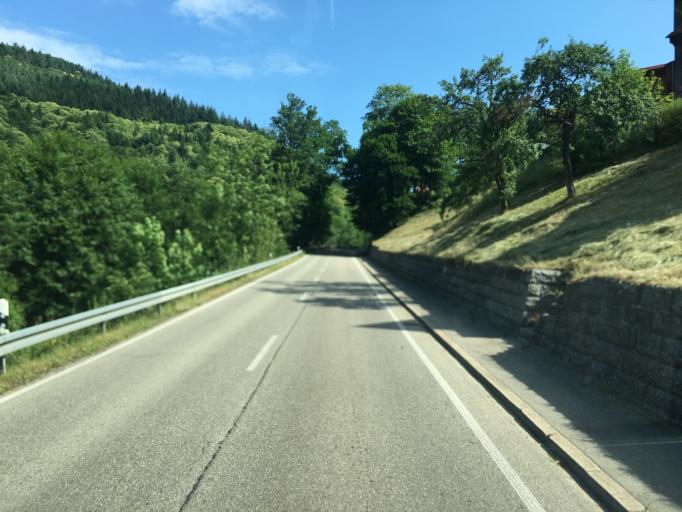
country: DE
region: Baden-Wuerttemberg
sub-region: Freiburg Region
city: Seebach
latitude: 48.5691
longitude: 8.1619
